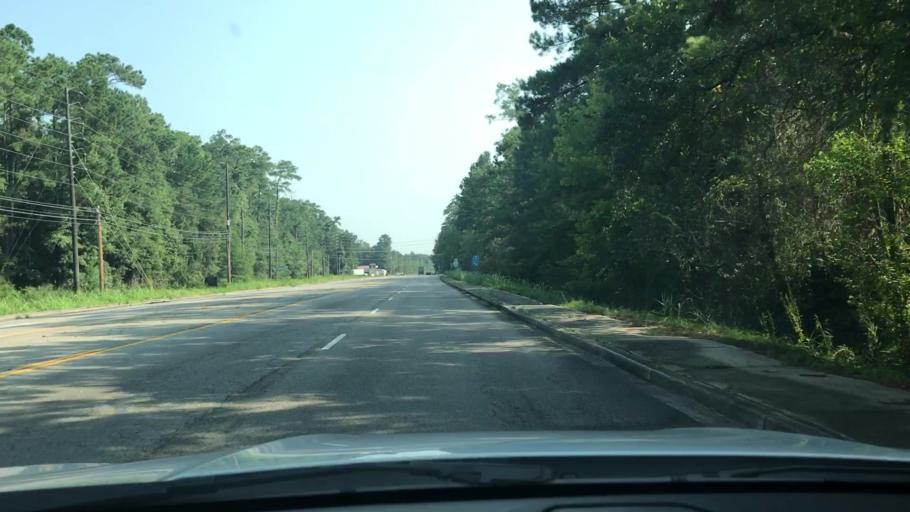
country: US
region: South Carolina
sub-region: Georgetown County
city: Georgetown
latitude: 33.4134
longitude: -79.2850
